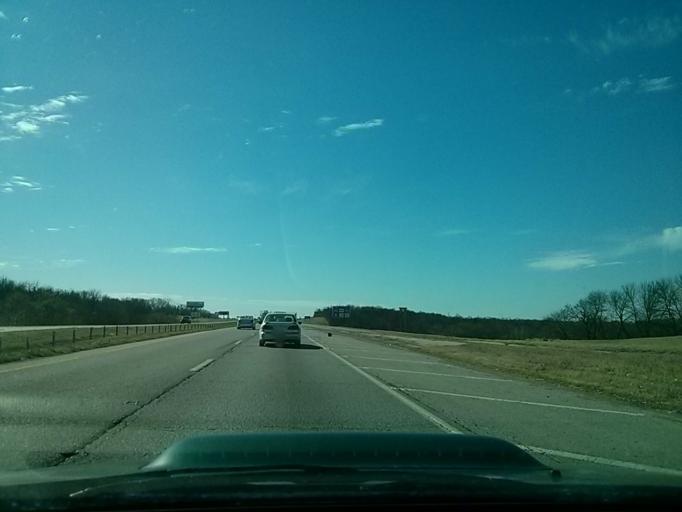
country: US
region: Oklahoma
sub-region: Tulsa County
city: Oakhurst
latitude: 36.0736
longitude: -96.0061
